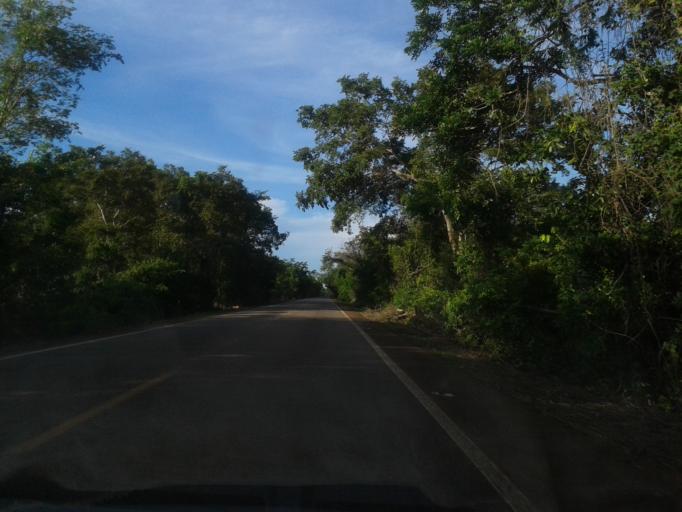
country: BR
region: Goias
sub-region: Sao Miguel Do Araguaia
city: Sao Miguel do Araguaia
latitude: -13.5248
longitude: -50.3040
